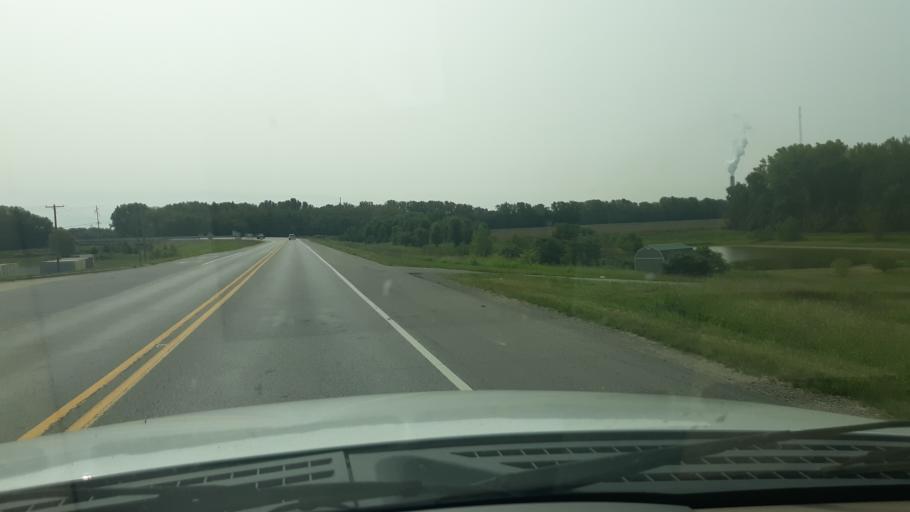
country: US
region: Illinois
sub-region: Wabash County
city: Mount Carmel
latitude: 38.4033
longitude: -87.7611
